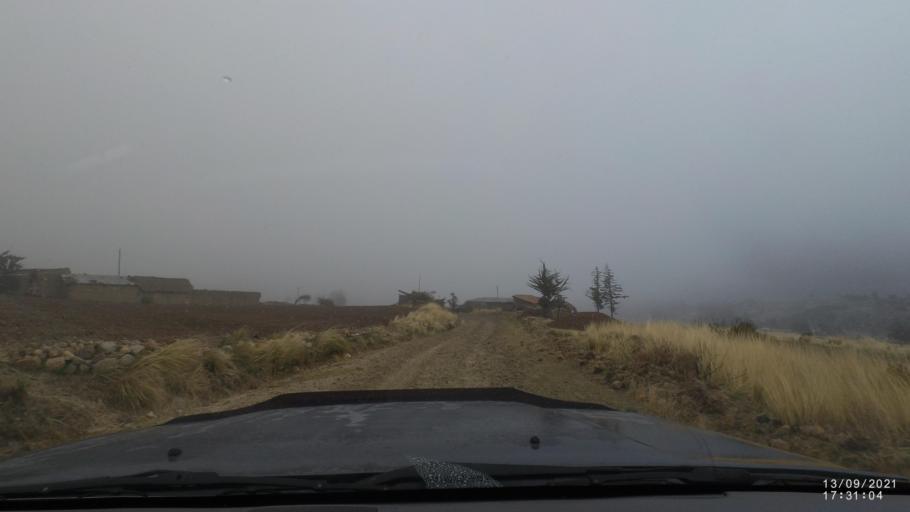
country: BO
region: Cochabamba
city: Colomi
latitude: -17.3611
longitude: -65.7890
